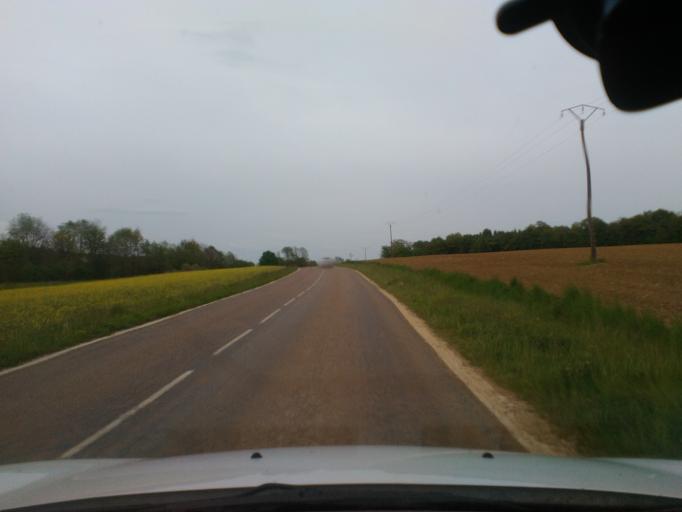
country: FR
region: Champagne-Ardenne
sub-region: Departement de la Haute-Marne
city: Bologne
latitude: 48.2120
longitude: 5.2094
